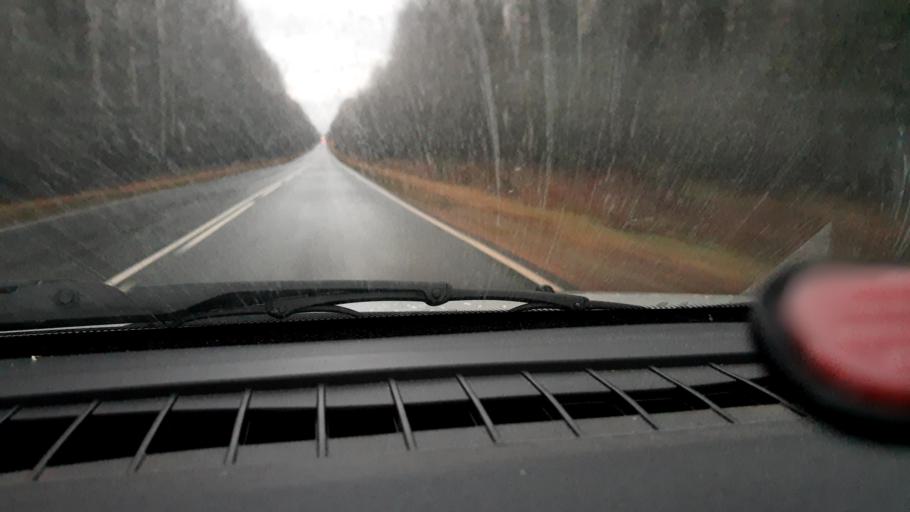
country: RU
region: Nizjnij Novgorod
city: Uren'
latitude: 57.2543
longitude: 45.6078
